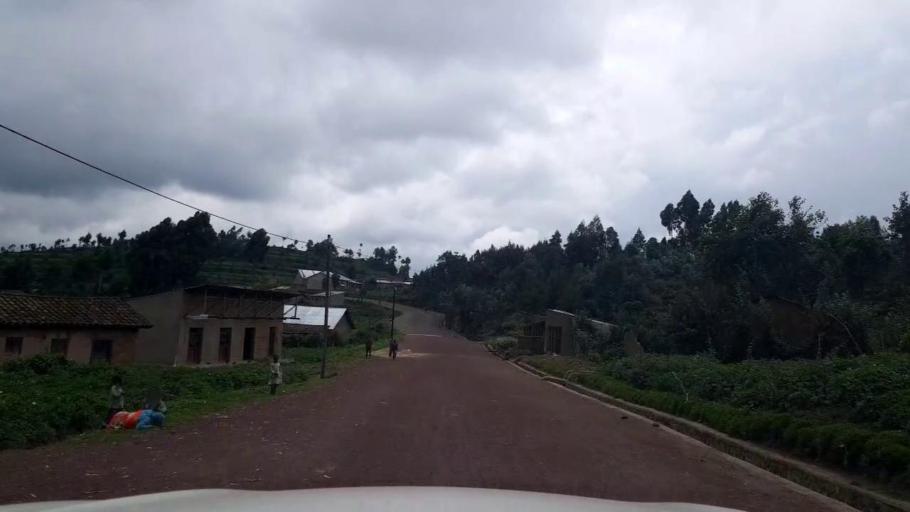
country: RW
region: Northern Province
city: Musanze
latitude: -1.5791
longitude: 29.4829
